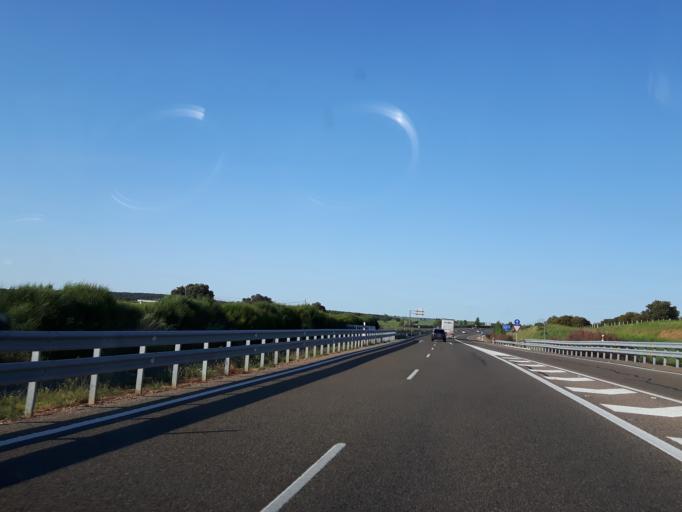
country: ES
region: Castille and Leon
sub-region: Provincia de Salamanca
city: Aldehuela de la Boveda
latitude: 40.8501
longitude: -6.0469
